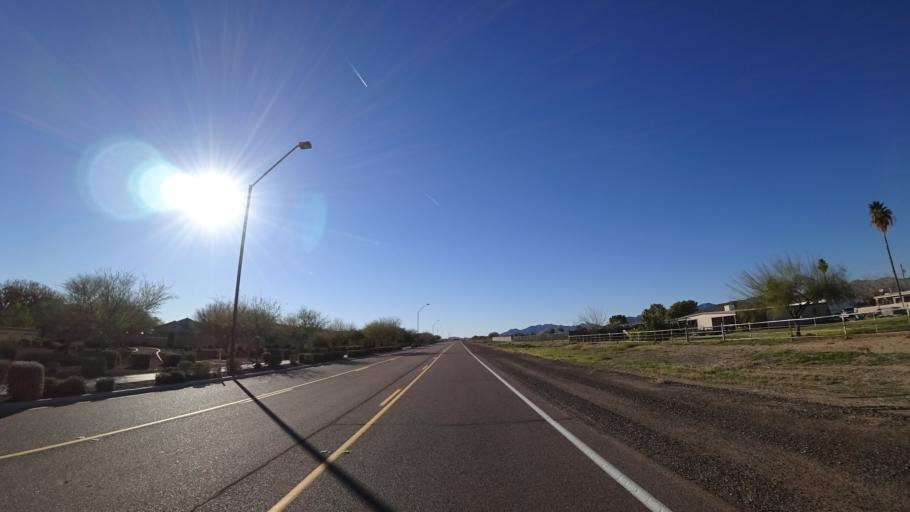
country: US
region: Arizona
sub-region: Maricopa County
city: Citrus Park
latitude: 33.4502
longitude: -112.4743
